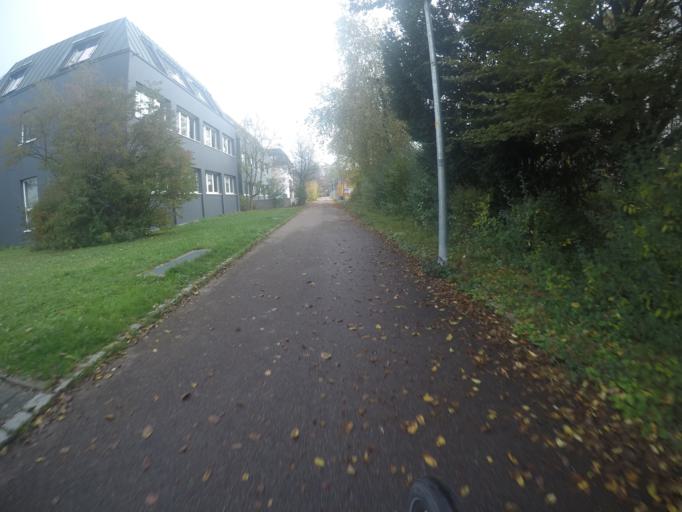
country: DE
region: Baden-Wuerttemberg
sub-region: Regierungsbezirk Stuttgart
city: Stuttgart
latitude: 48.7480
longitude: 9.1629
